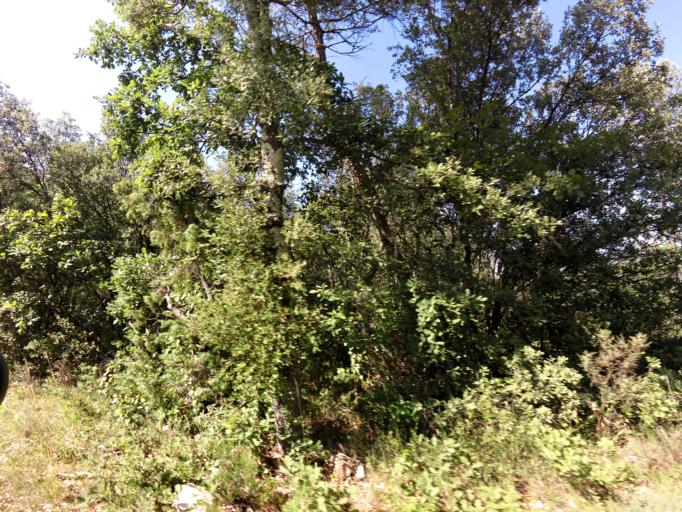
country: FR
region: Languedoc-Roussillon
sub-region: Departement du Gard
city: Quissac
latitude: 43.8813
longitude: 4.0295
